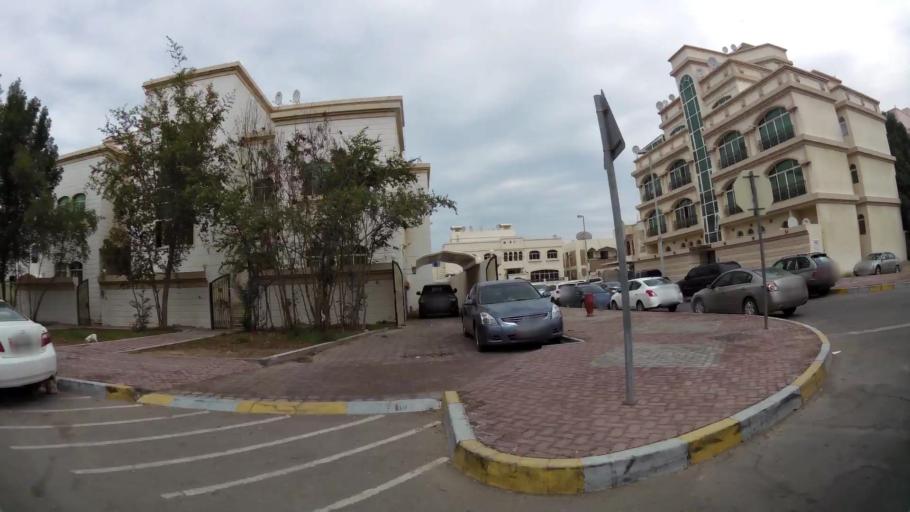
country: AE
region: Abu Dhabi
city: Abu Dhabi
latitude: 24.4397
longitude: 54.4043
